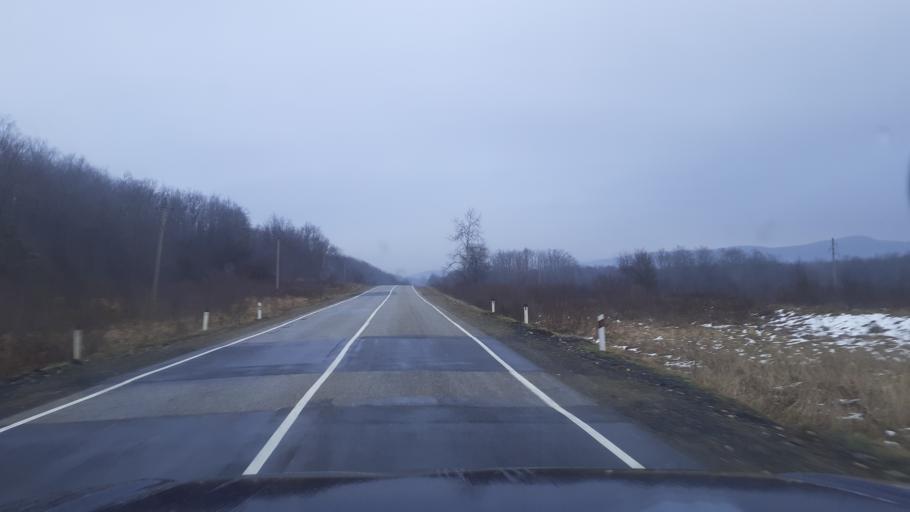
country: RU
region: Krasnodarskiy
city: Neftegorsk
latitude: 44.2725
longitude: 39.7864
